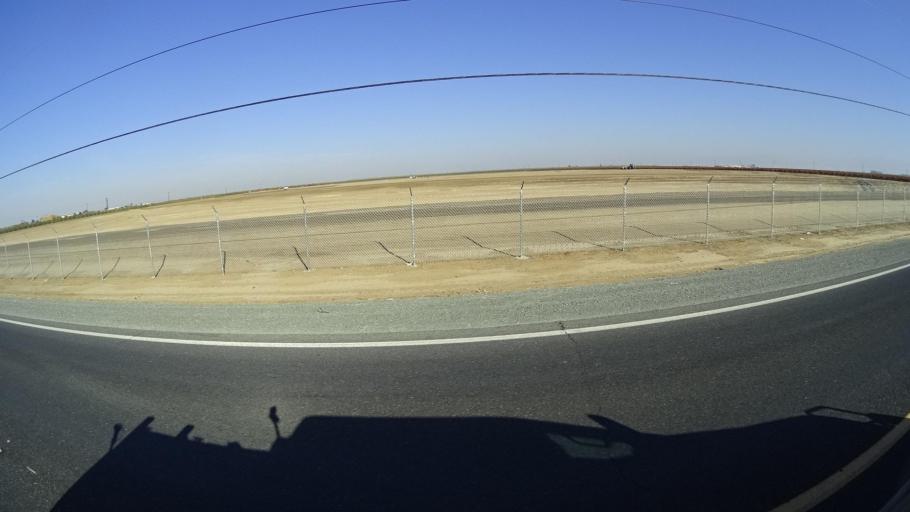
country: US
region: California
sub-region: Kern County
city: Delano
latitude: 35.7614
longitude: -119.2116
